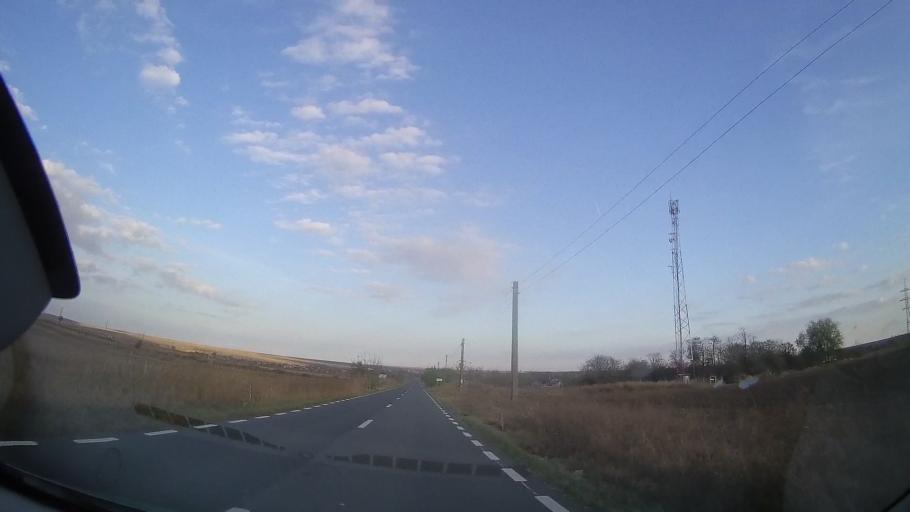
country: RO
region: Constanta
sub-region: Comuna Chirnogeni
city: Plopeni
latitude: 43.9512
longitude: 28.1753
